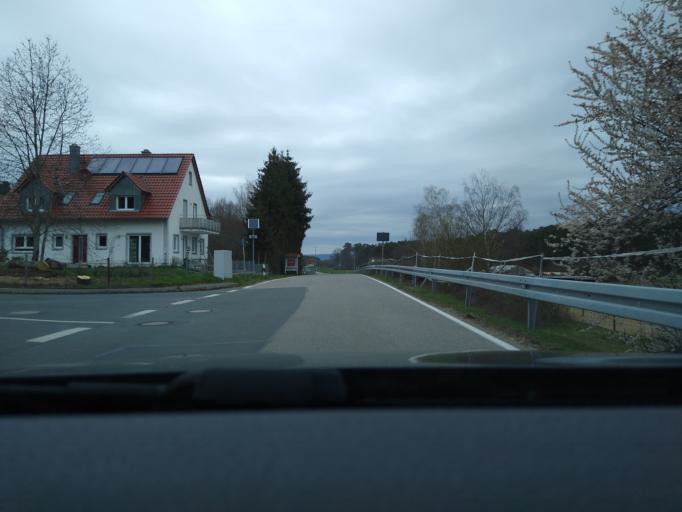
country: DE
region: Bavaria
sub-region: Regierungsbezirk Mittelfranken
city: Mohrendorf
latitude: 49.6543
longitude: 11.0083
